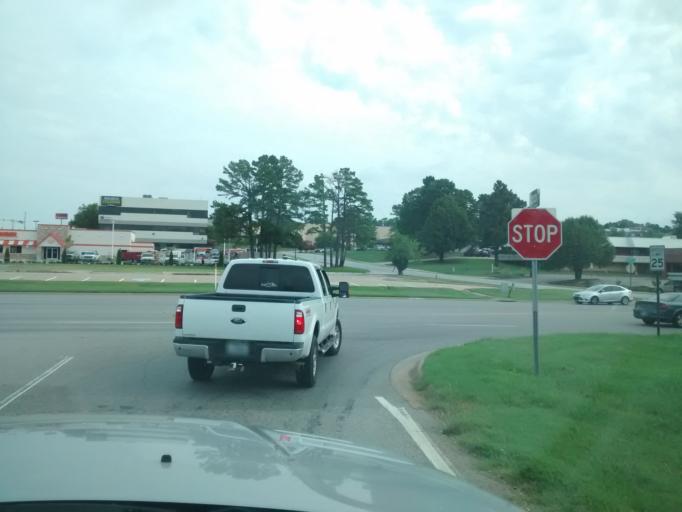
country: US
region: Arkansas
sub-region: Washington County
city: Johnson
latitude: 36.1232
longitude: -94.1438
